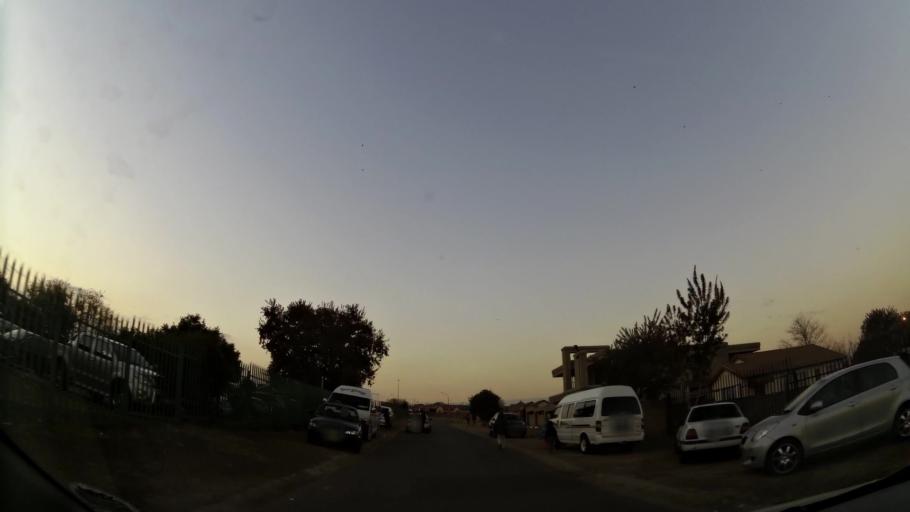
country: ZA
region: Gauteng
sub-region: West Rand District Municipality
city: Randfontein
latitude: -26.2112
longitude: 27.7136
